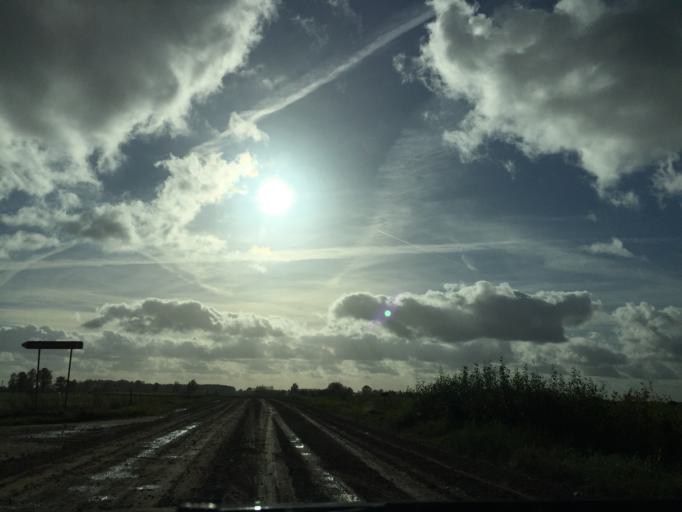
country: LV
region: Lielvarde
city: Lielvarde
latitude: 56.7398
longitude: 24.9001
